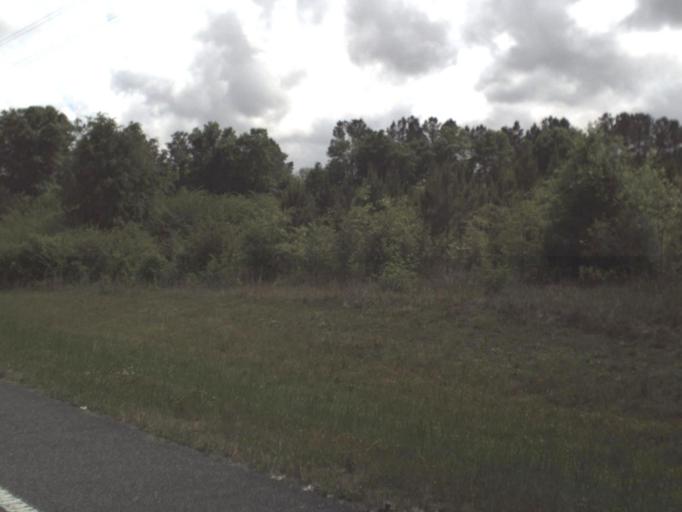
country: US
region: Florida
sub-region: Santa Rosa County
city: Wallace
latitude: 30.8160
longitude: -87.1323
